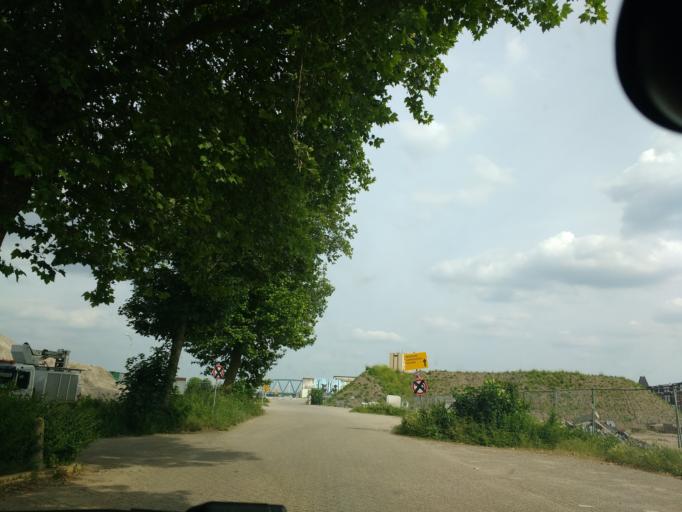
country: NL
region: Gelderland
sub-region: Gemeente Nijmegen
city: Nijmegen
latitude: 51.8554
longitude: 5.8418
